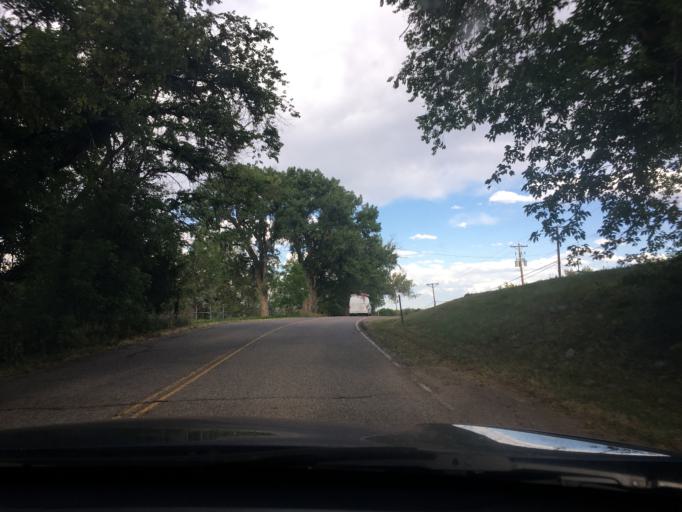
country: US
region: Colorado
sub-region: Jefferson County
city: Applewood
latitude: 39.7618
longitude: -105.1800
